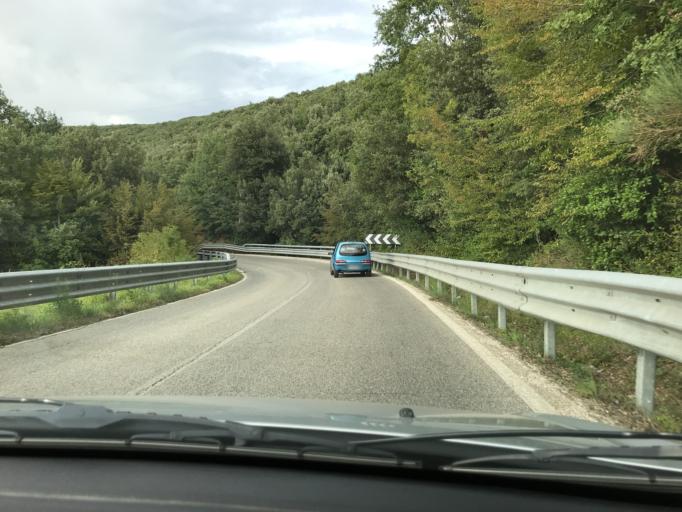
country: IT
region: Umbria
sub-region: Provincia di Terni
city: Guardea
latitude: 42.6376
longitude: 12.2919
